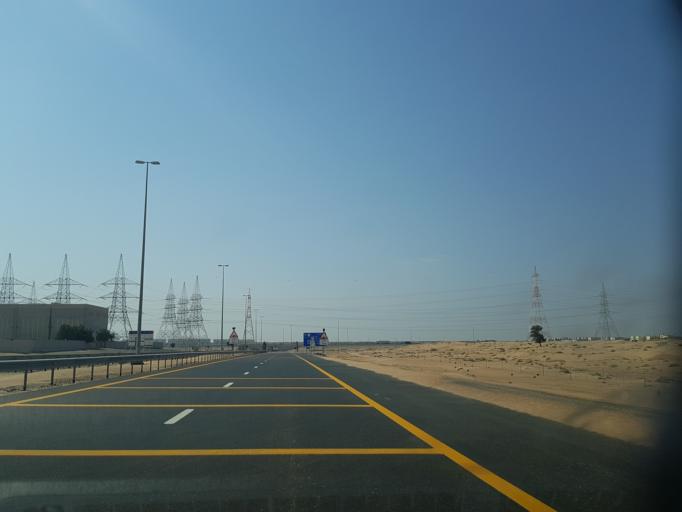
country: AE
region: Ash Shariqah
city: Sharjah
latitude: 25.2852
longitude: 55.5939
